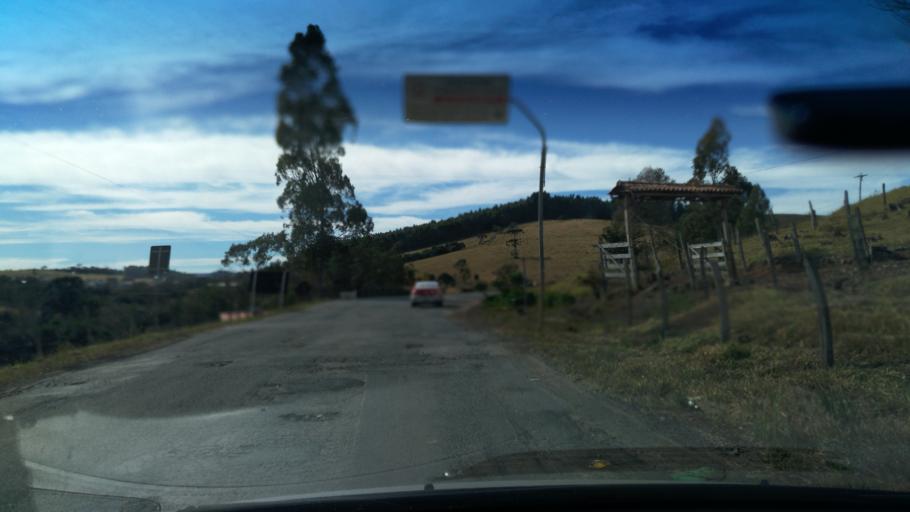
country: BR
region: Minas Gerais
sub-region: Andradas
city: Andradas
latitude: -22.0386
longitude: -46.3493
